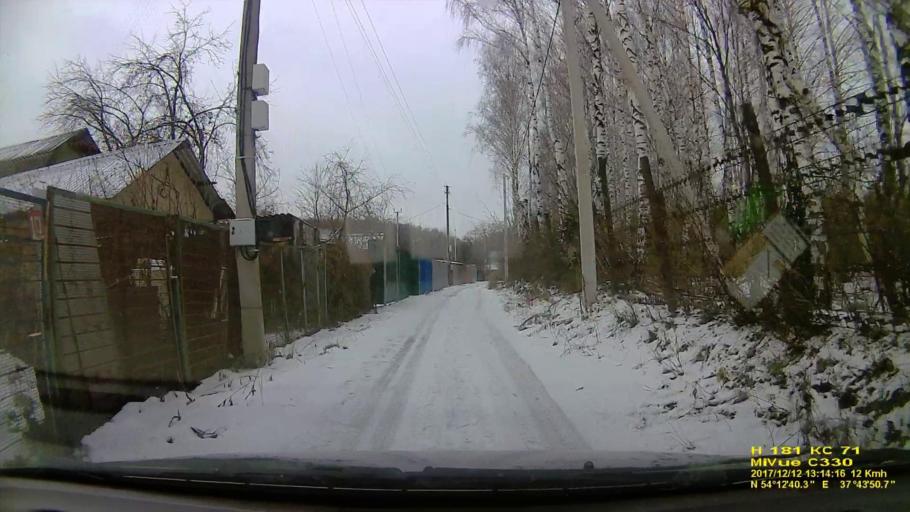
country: RU
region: Tula
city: Tula
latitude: 54.2112
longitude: 37.7307
